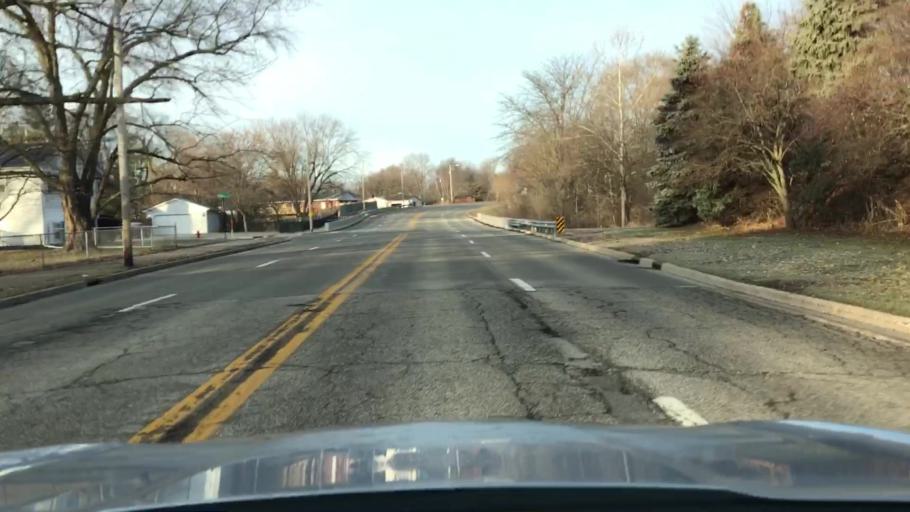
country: US
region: Illinois
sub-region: McLean County
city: Normal
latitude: 40.5027
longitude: -88.9614
